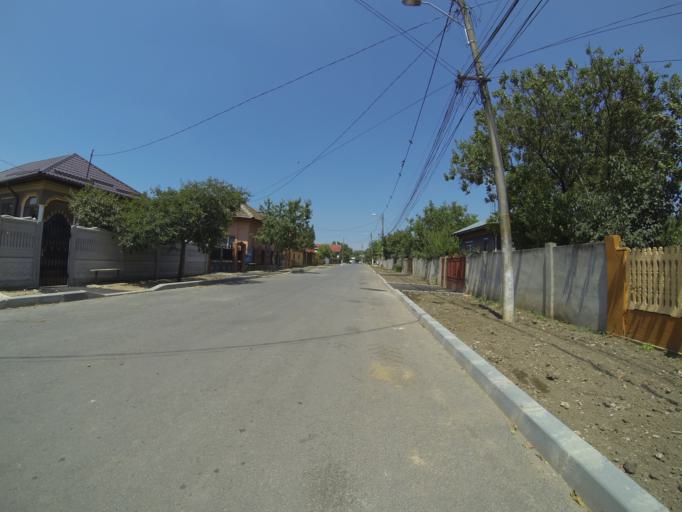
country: RO
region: Dolj
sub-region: Comuna Segarcea
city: Segarcea
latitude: 44.0887
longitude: 23.7418
